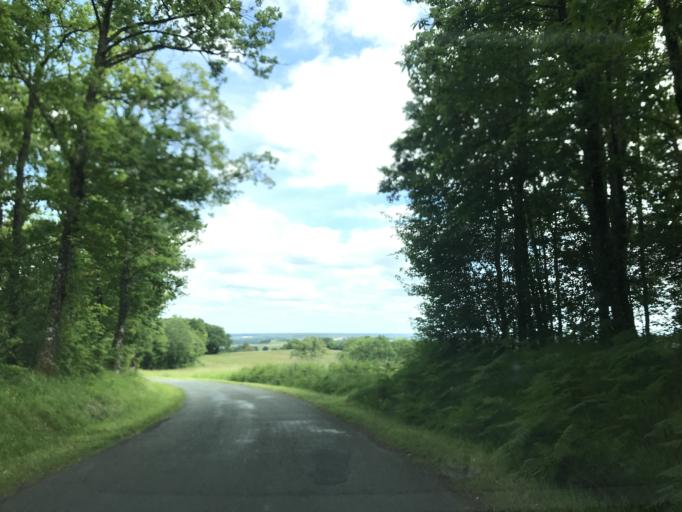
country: FR
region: Poitou-Charentes
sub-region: Departement de la Charente
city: Chalais
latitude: 45.2729
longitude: 0.1110
